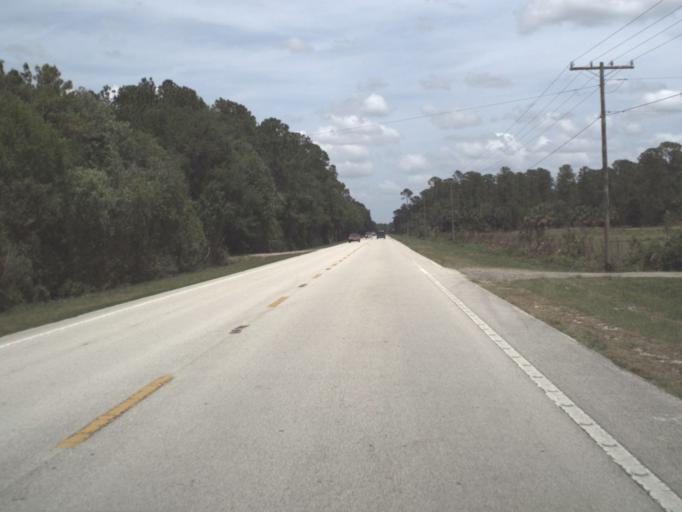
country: US
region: Florida
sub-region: Lake County
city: Lake Mack-Forest Hills
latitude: 28.9795
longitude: -81.4036
